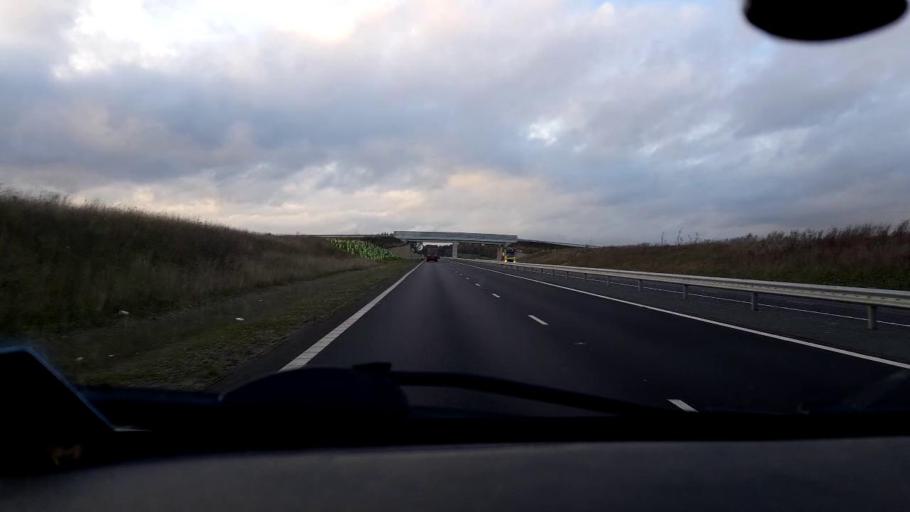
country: GB
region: England
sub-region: Norfolk
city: Horsford
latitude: 52.6920
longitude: 1.2274
